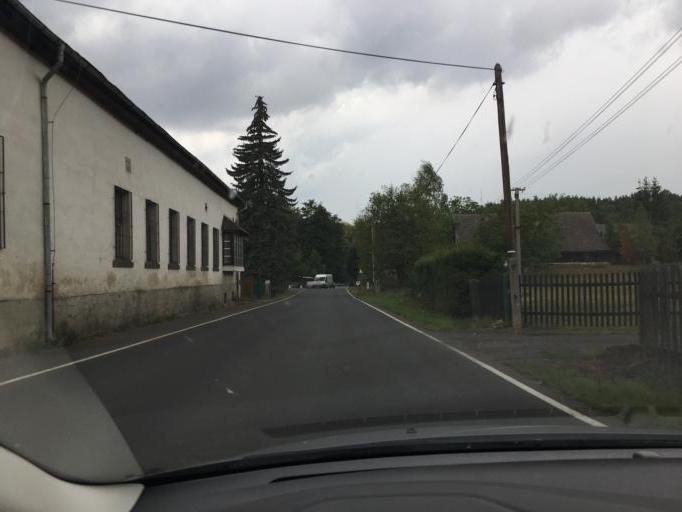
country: CZ
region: Ustecky
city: Ceska Kamenice
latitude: 50.8046
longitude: 14.3643
